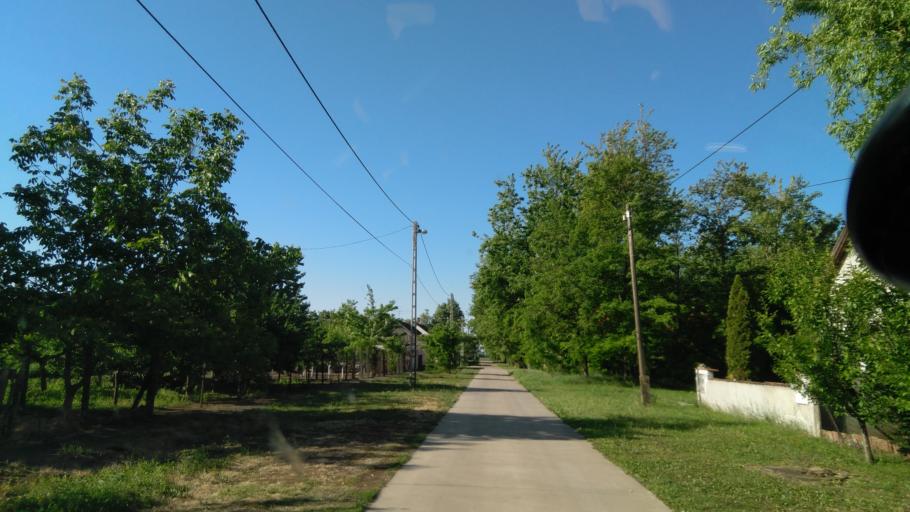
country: HU
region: Bekes
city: Elek
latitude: 46.5320
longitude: 21.2329
